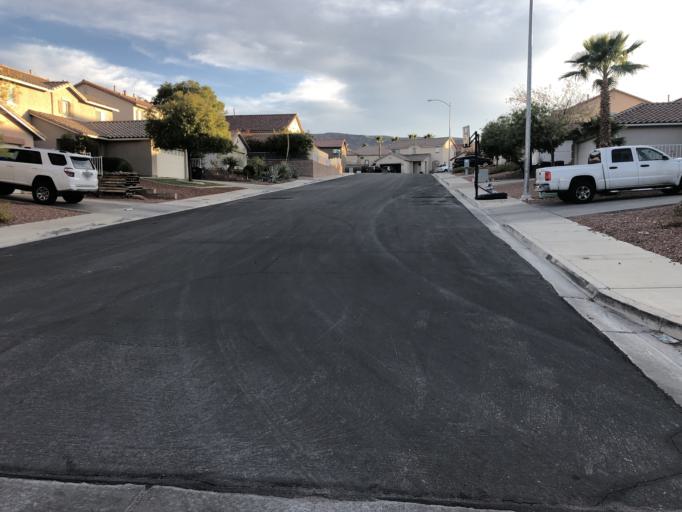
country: US
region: Nevada
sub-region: Clark County
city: Whitney
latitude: 36.0165
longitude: -115.0450
